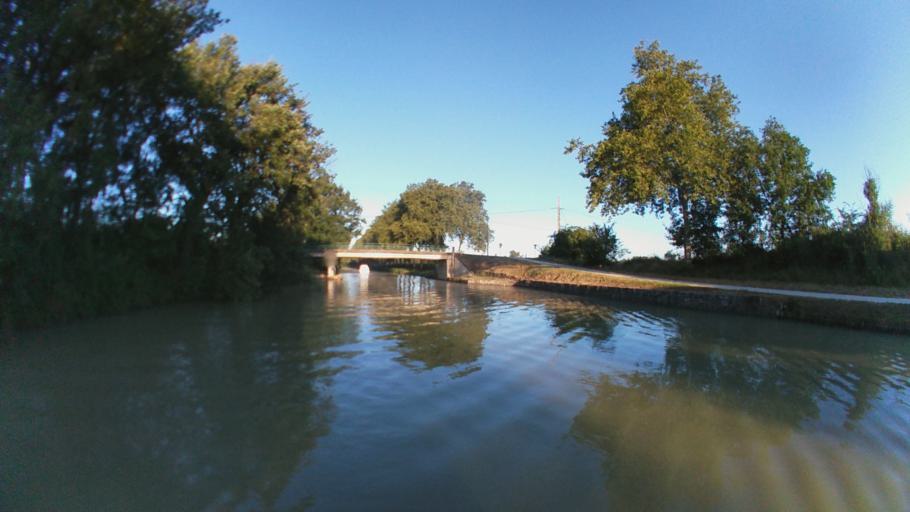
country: FR
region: Midi-Pyrenees
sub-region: Departement de la Haute-Garonne
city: Villenouvelle
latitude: 43.4121
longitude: 1.6577
